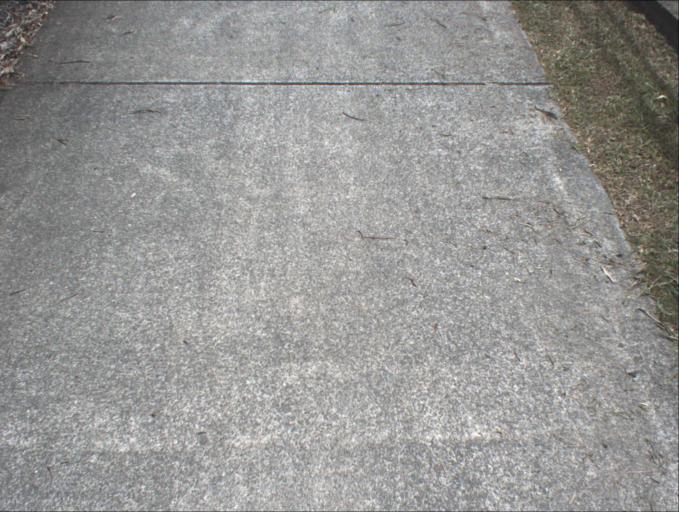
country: AU
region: Queensland
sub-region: Logan
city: Slacks Creek
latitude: -27.6335
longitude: 153.1553
